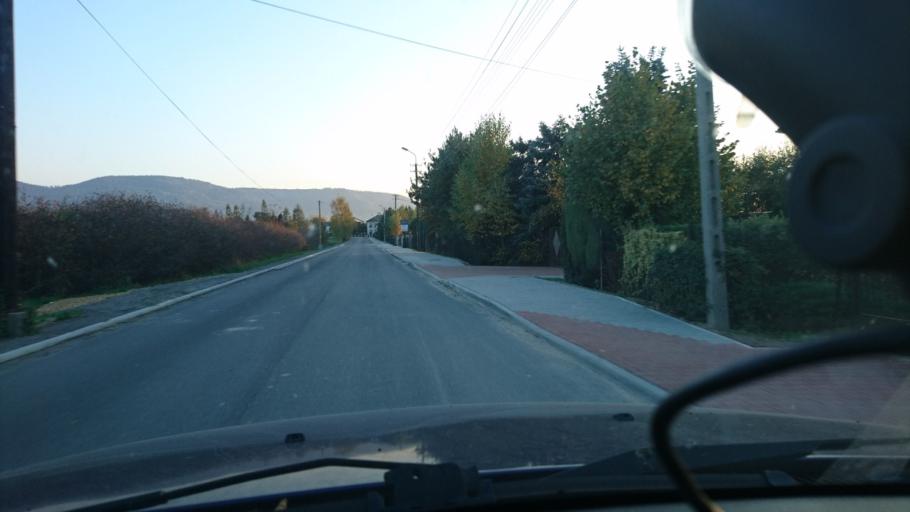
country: PL
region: Silesian Voivodeship
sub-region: Powiat bielski
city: Kozy
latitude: 49.8611
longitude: 19.1338
